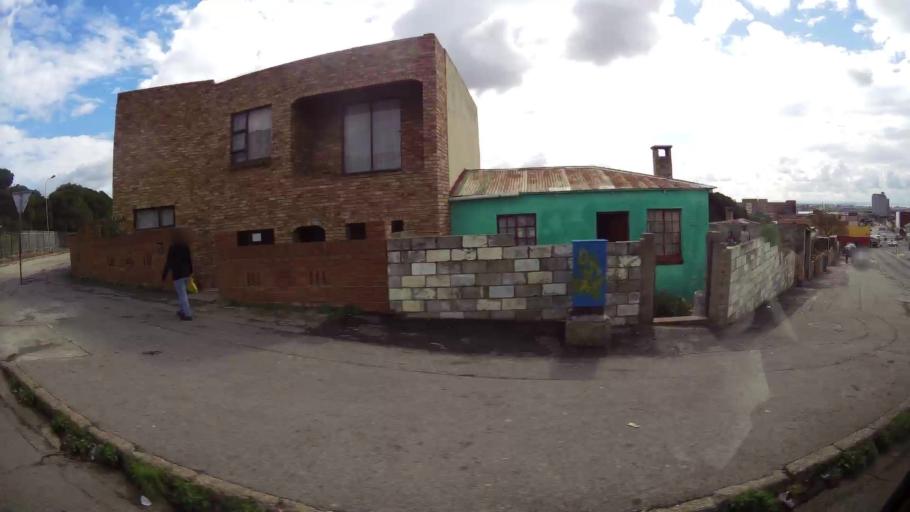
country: ZA
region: Eastern Cape
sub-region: Nelson Mandela Bay Metropolitan Municipality
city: Port Elizabeth
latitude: -33.9298
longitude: 25.5684
